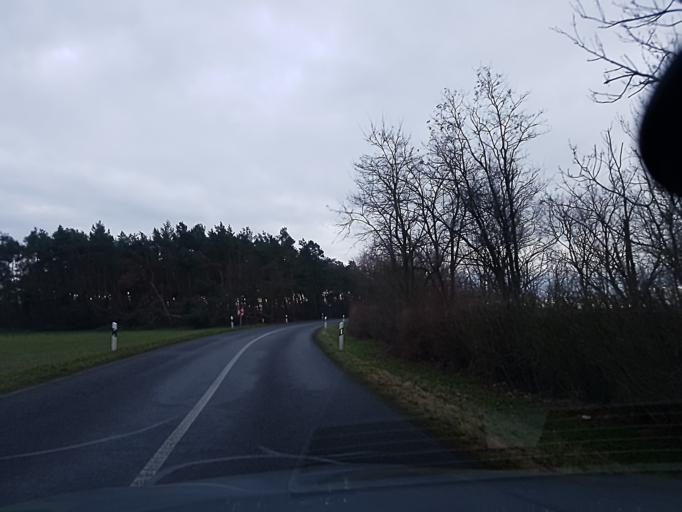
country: DE
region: Brandenburg
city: Bad Liebenwerda
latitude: 51.5413
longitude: 13.3148
